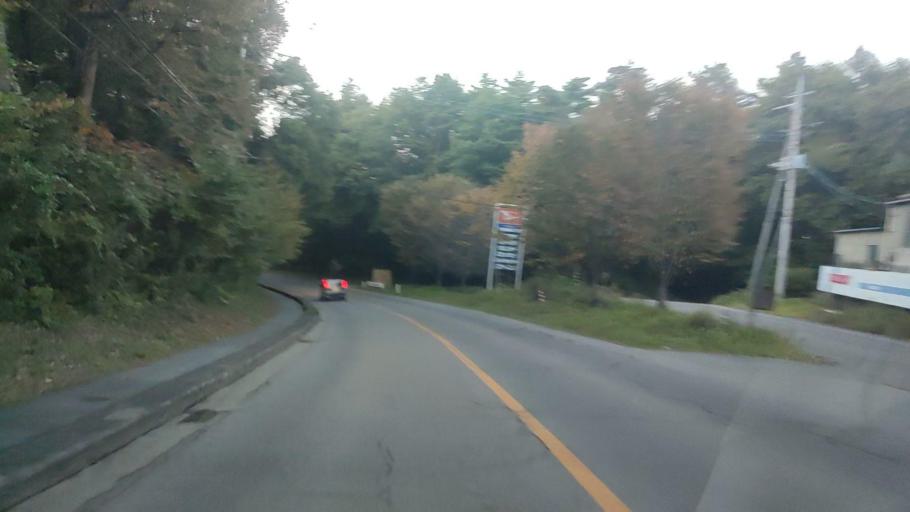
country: JP
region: Nagano
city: Komoro
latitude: 36.4778
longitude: 138.5870
